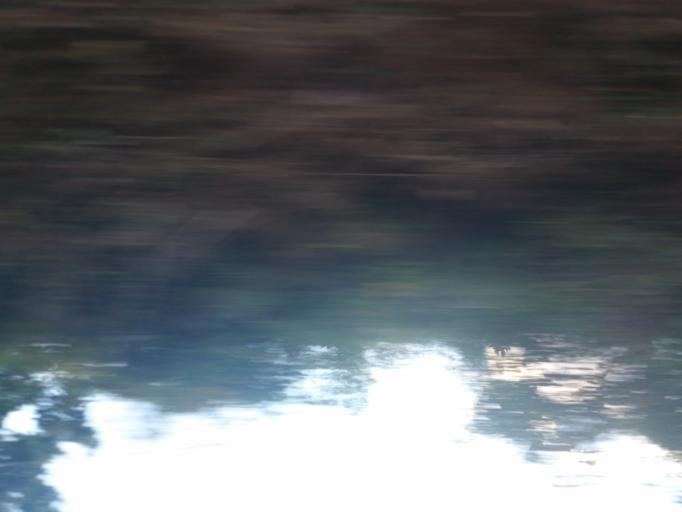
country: US
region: Tennessee
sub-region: Blount County
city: Louisville
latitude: 35.7800
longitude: -84.0570
